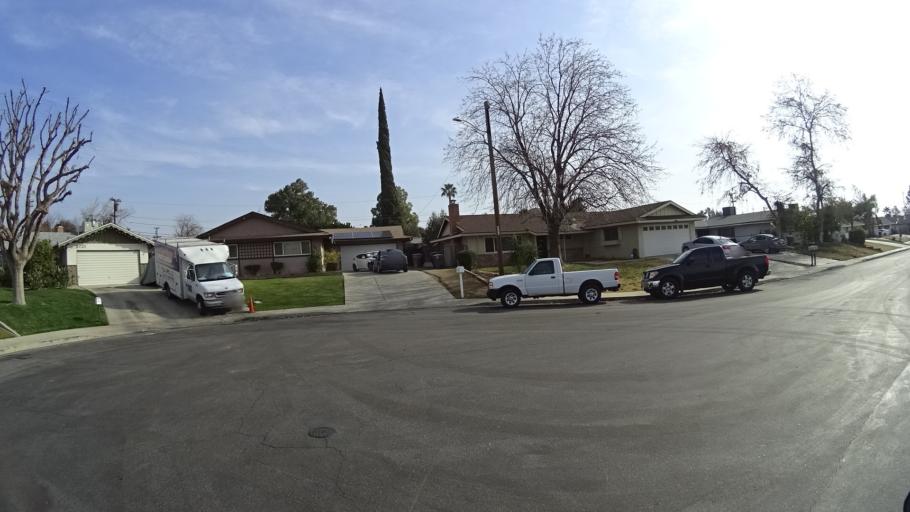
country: US
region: California
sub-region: Kern County
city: Oildale
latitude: 35.3990
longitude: -118.9635
